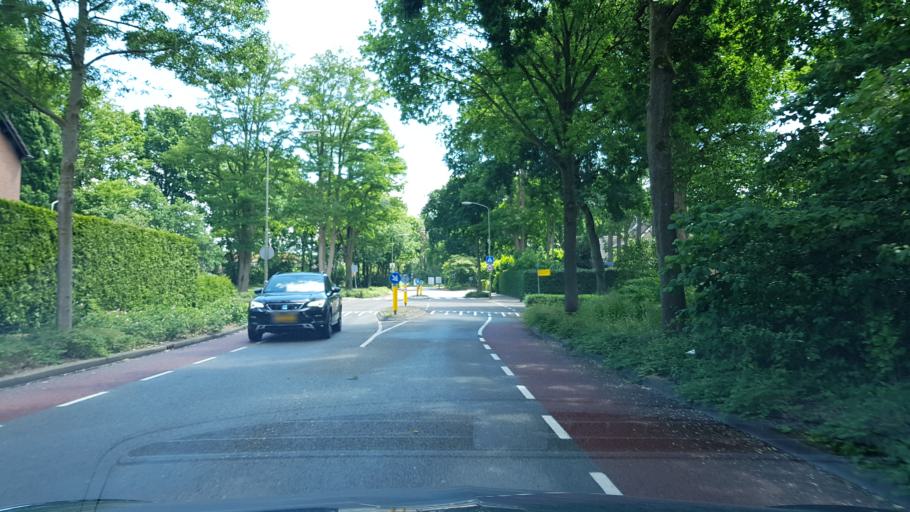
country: NL
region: Gelderland
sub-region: Gemeente Nunspeet
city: Nunspeet
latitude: 52.3698
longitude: 5.7634
